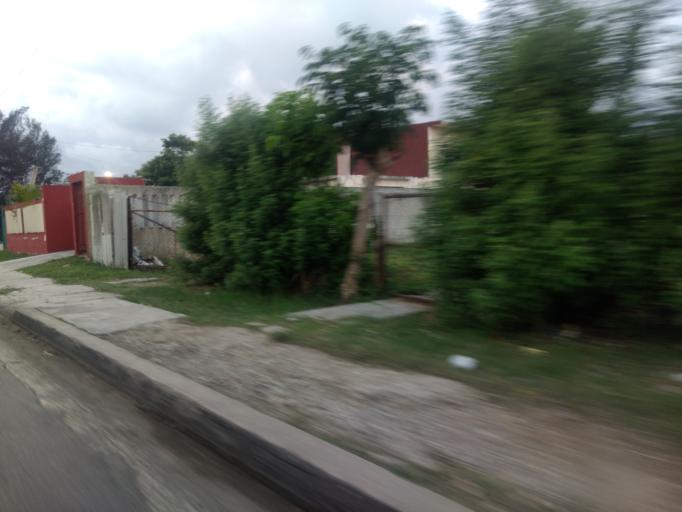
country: CU
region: Artemisa
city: Bauta
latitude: 23.0792
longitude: -82.5074
